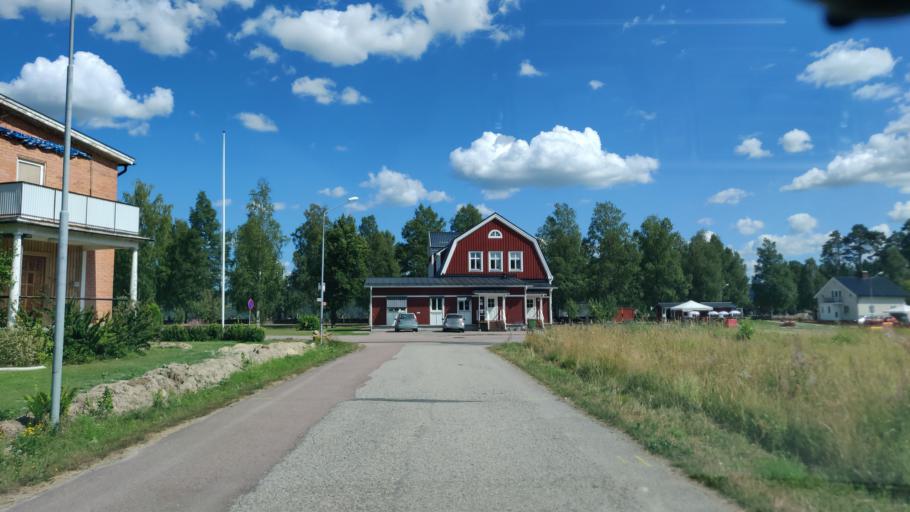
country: SE
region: Vaermland
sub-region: Hagfors Kommun
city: Ekshaerad
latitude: 60.1716
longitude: 13.4946
